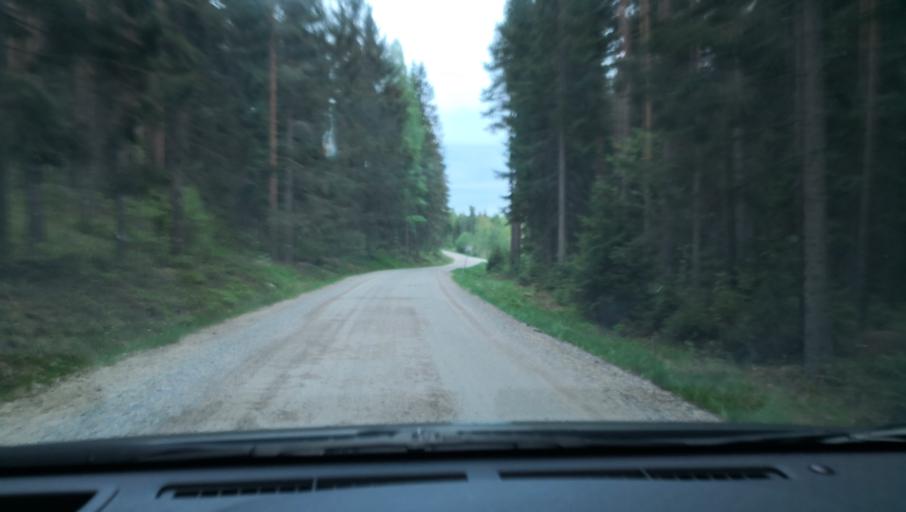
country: SE
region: Vaestmanland
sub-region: Skinnskattebergs Kommun
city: Skinnskatteberg
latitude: 59.7514
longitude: 15.4571
